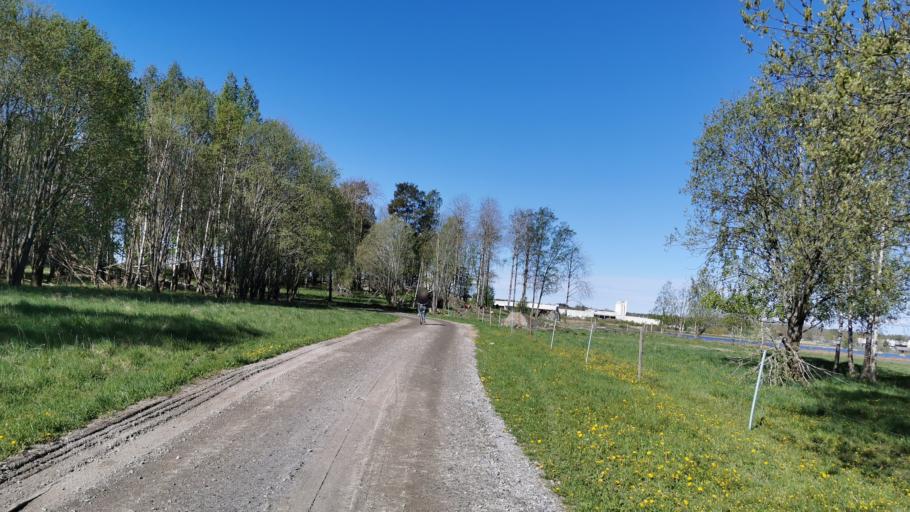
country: SE
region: OErebro
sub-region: Orebro Kommun
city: Orebro
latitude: 59.2984
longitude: 15.2204
